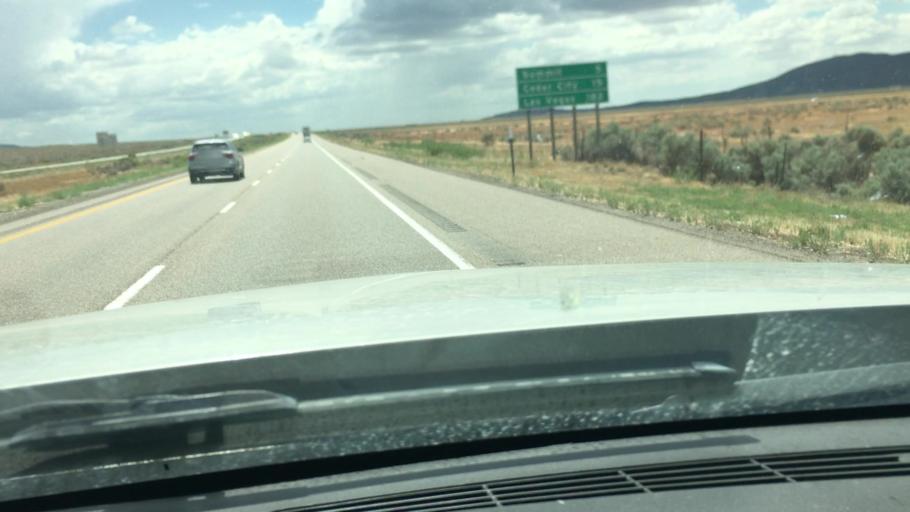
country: US
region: Utah
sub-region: Iron County
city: Parowan
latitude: 37.8334
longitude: -112.8861
